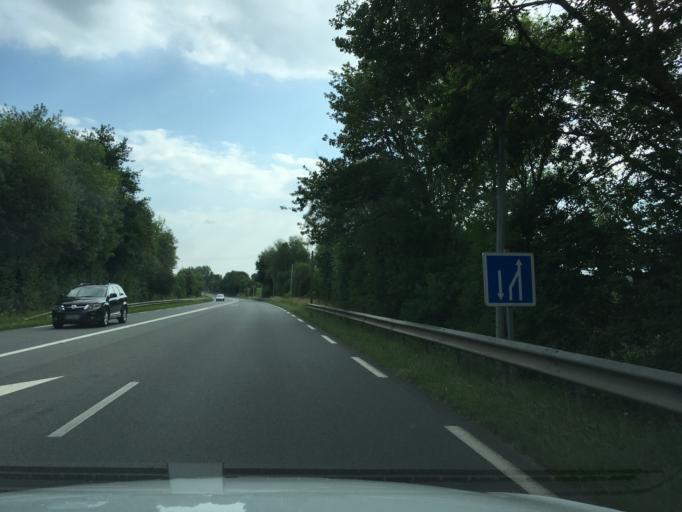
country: FR
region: Poitou-Charentes
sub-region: Departement des Deux-Sevres
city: Le Tallud
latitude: 46.6237
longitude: -0.2795
